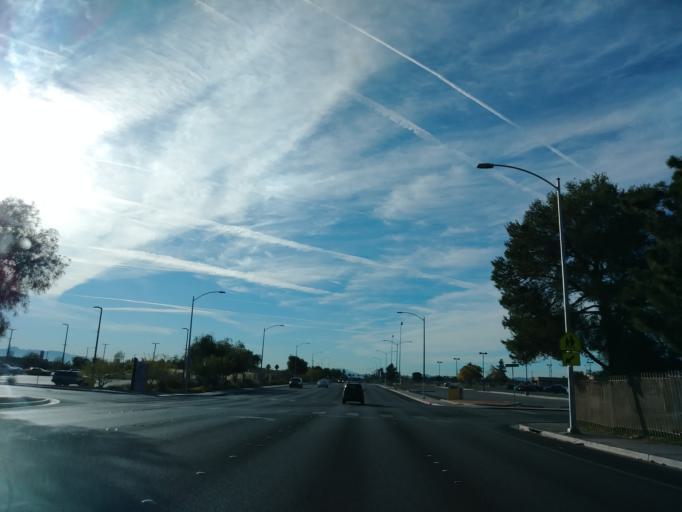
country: US
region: Nevada
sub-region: Clark County
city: Spring Valley
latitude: 36.1558
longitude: -115.2347
